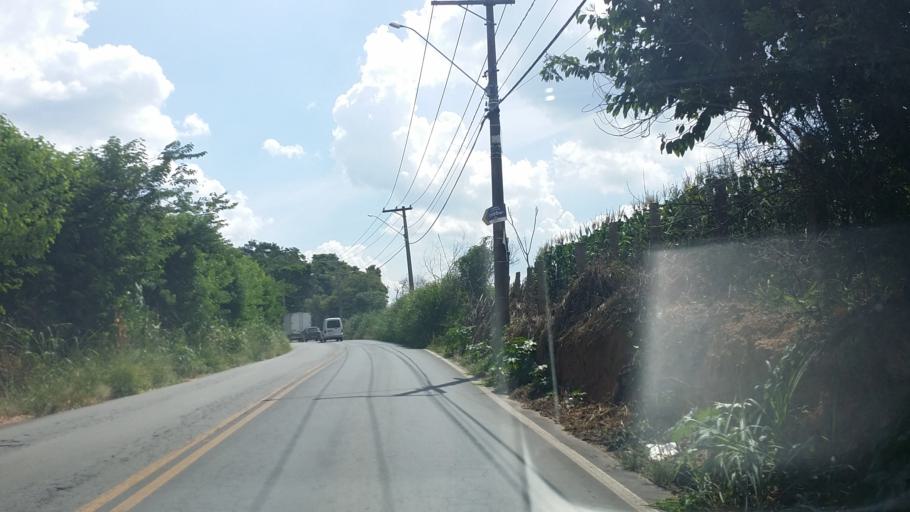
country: BR
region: Sao Paulo
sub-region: Itupeva
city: Itupeva
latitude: -23.1805
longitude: -47.0630
